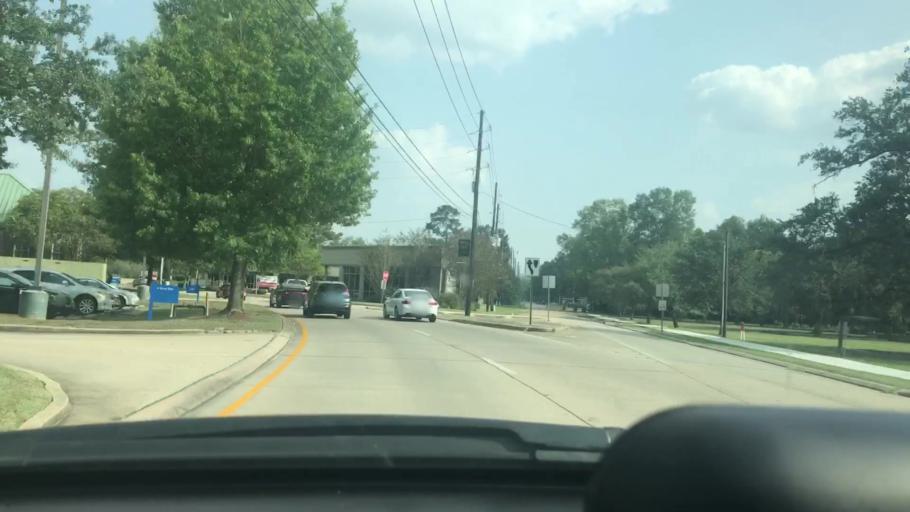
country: US
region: Louisiana
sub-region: Tangipahoa Parish
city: Hammond
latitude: 30.4989
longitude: -90.4608
